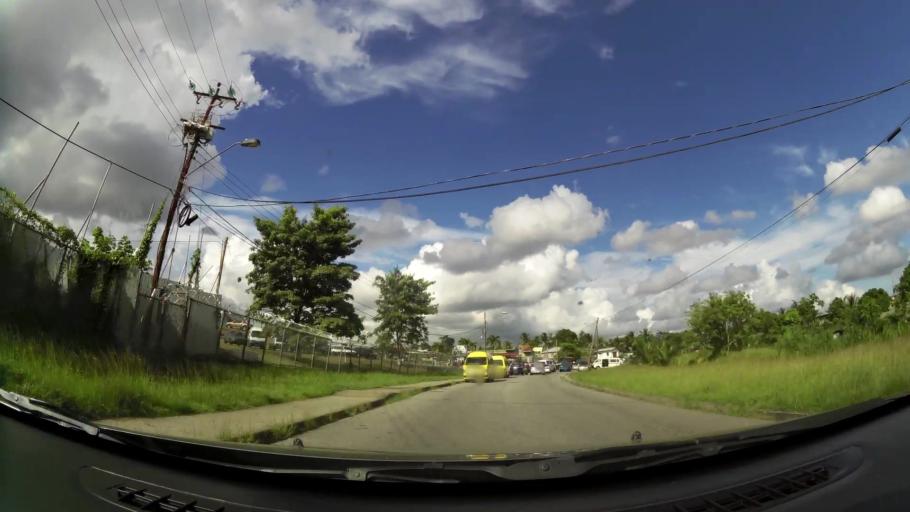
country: TT
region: City of San Fernando
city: Mon Repos
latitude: 10.2708
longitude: -61.4484
